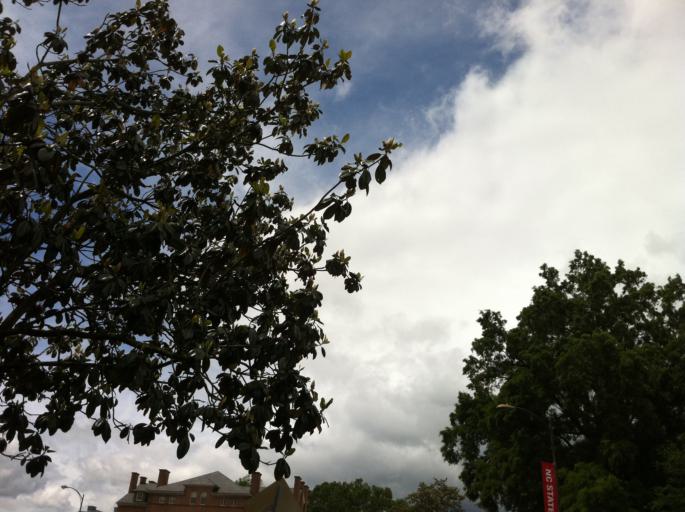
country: US
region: North Carolina
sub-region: Wake County
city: West Raleigh
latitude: 35.7858
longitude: -78.6628
